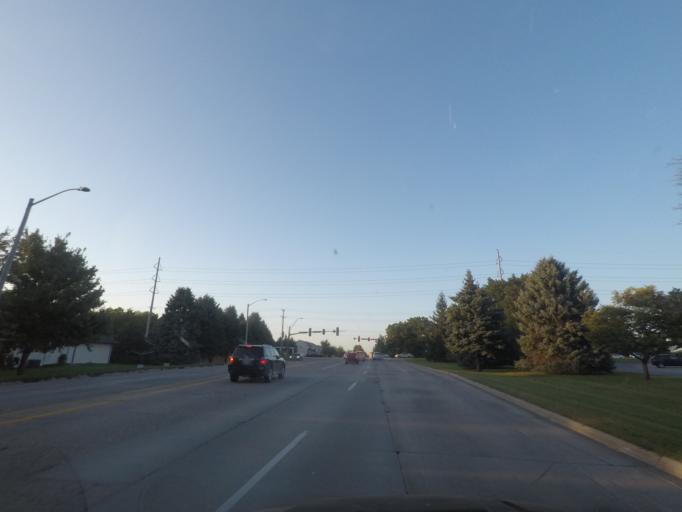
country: US
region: Iowa
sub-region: Story County
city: Ames
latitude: 42.0445
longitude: -93.6448
